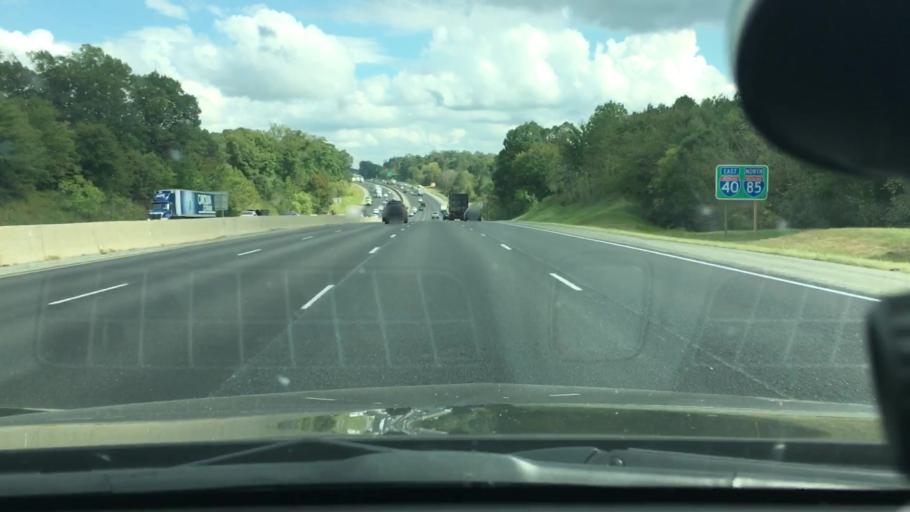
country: US
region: North Carolina
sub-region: Guilford County
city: Gibsonville
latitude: 36.0603
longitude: -79.5990
